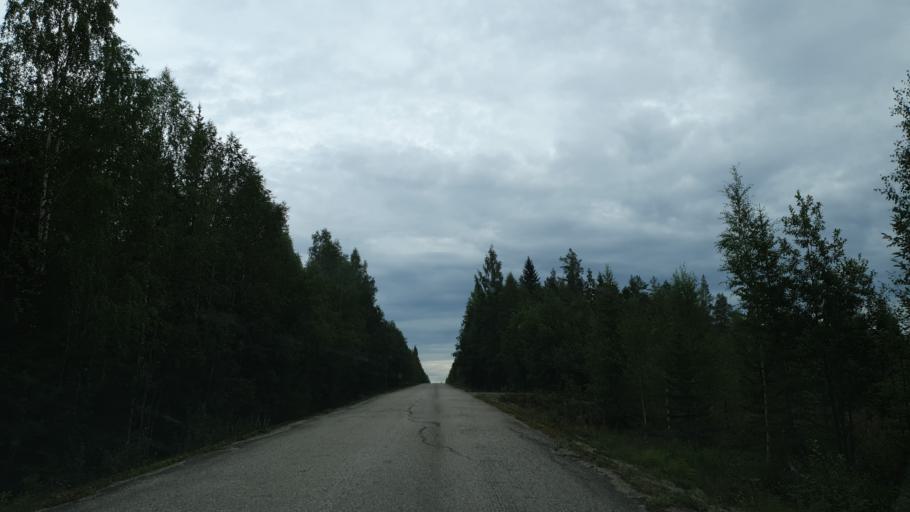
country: FI
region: Kainuu
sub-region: Kehys-Kainuu
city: Kuhmo
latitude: 64.3514
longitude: 29.1156
